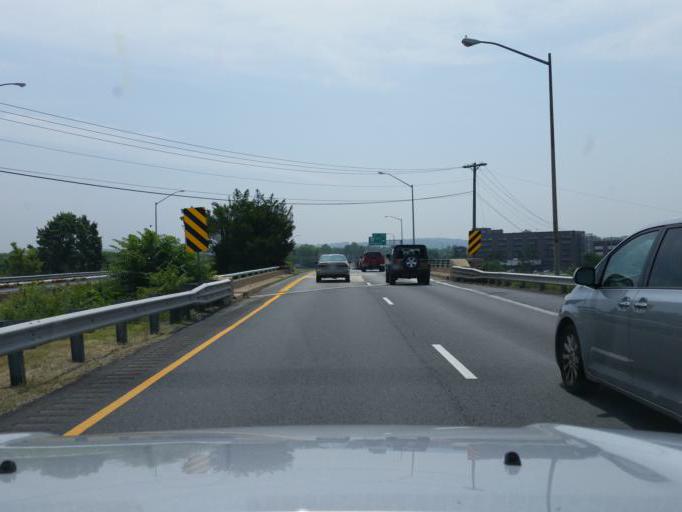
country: US
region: Maryland
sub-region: Frederick County
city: Ballenger Creek
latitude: 39.3821
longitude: -77.4100
